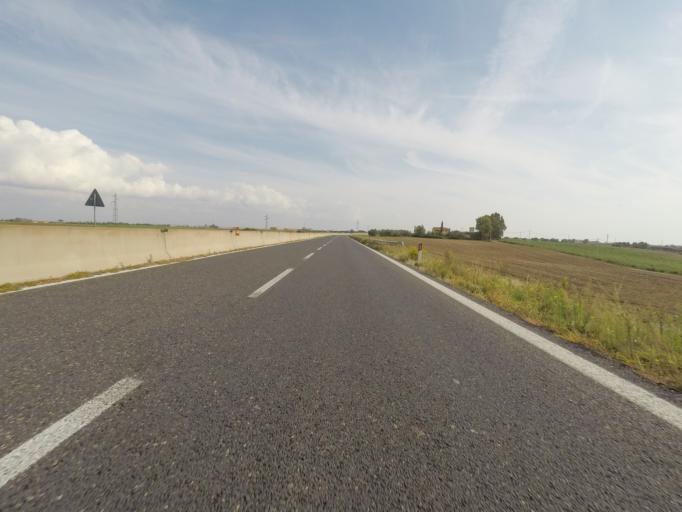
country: IT
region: Latium
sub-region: Provincia di Viterbo
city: Montalto di Castro
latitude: 42.3637
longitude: 11.5805
